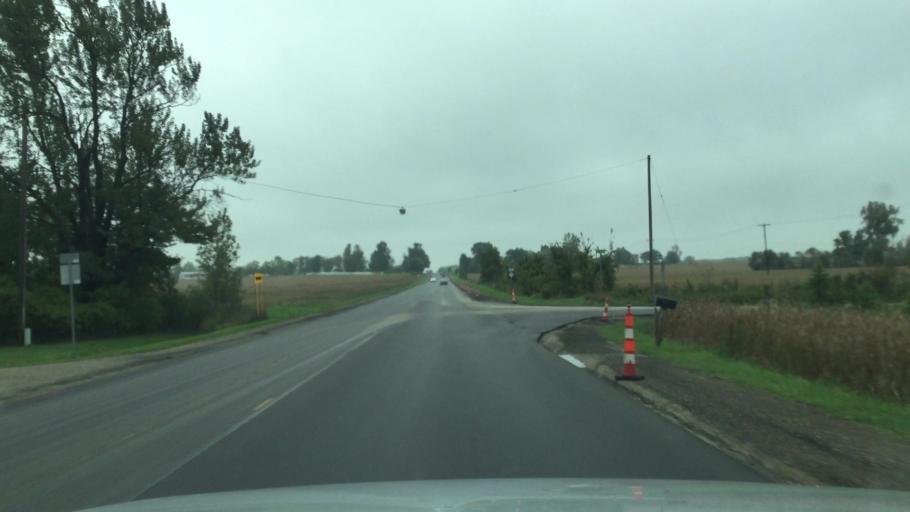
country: US
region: Michigan
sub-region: Shiawassee County
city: Perry
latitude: 42.8711
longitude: -84.2214
